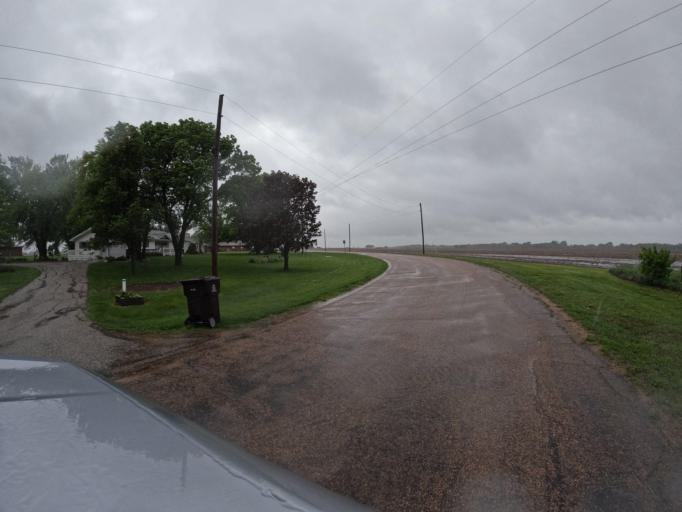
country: US
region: Nebraska
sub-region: Gage County
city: Wymore
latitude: 40.1248
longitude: -96.6758
